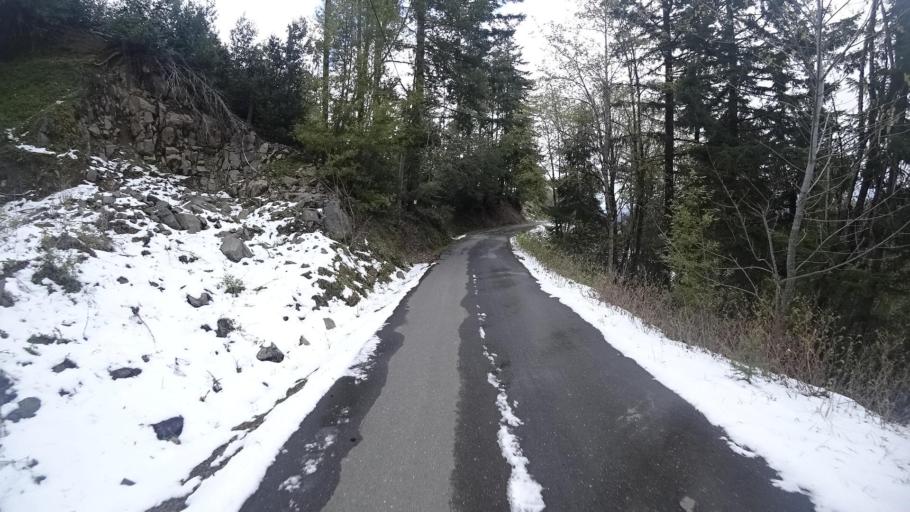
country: US
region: California
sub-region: Humboldt County
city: Blue Lake
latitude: 40.8812
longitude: -123.8730
